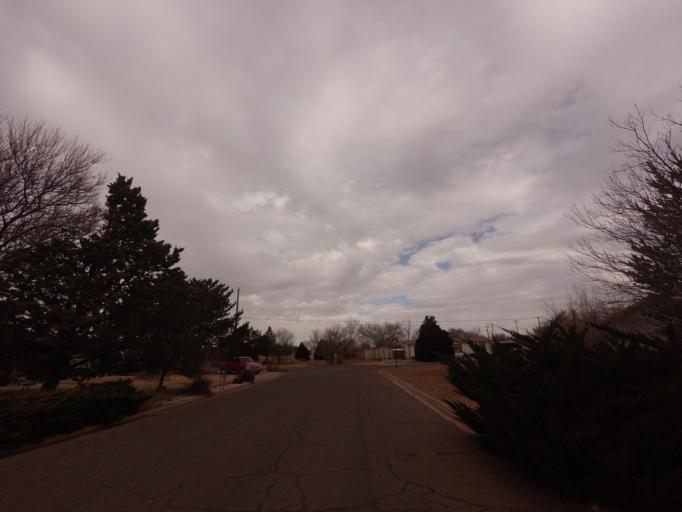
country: US
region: New Mexico
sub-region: Curry County
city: Clovis
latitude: 34.3797
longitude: -103.2022
